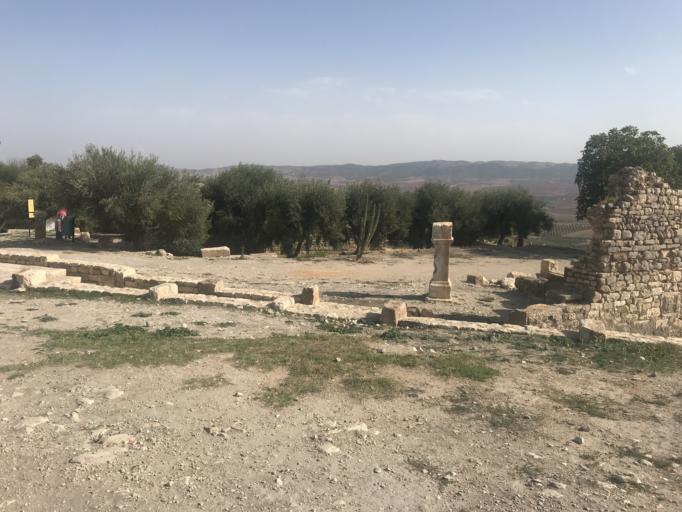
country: TN
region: Bajah
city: Tabursuq
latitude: 36.4232
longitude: 9.2198
